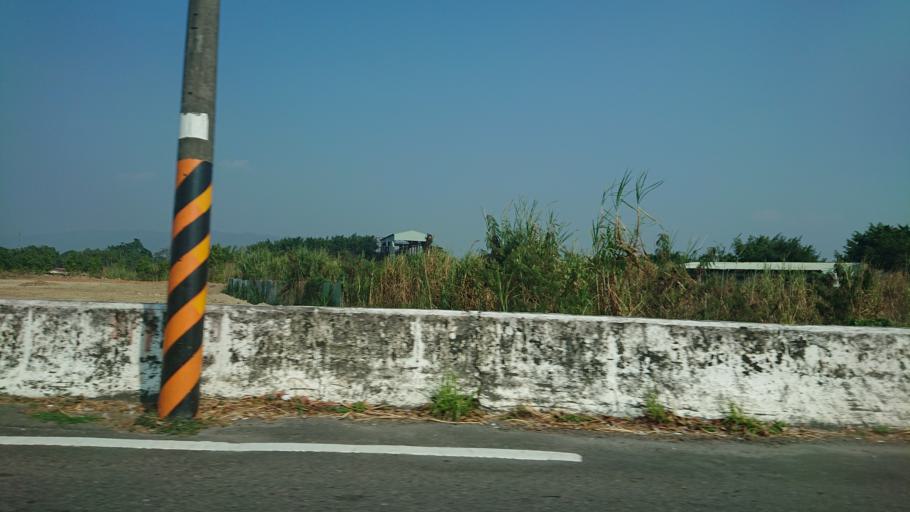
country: TW
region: Taiwan
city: Lugu
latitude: 23.7586
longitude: 120.6605
